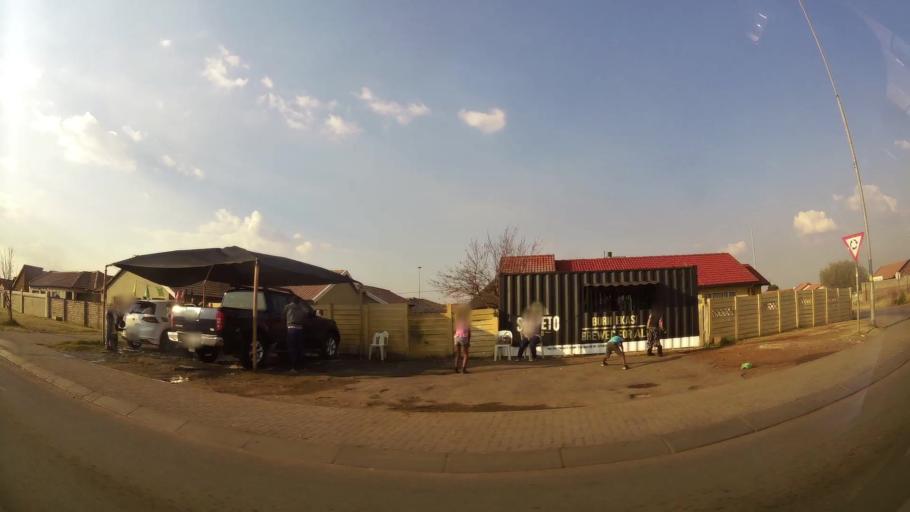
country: ZA
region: Gauteng
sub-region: Ekurhuleni Metropolitan Municipality
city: Germiston
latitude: -26.3479
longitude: 28.2190
